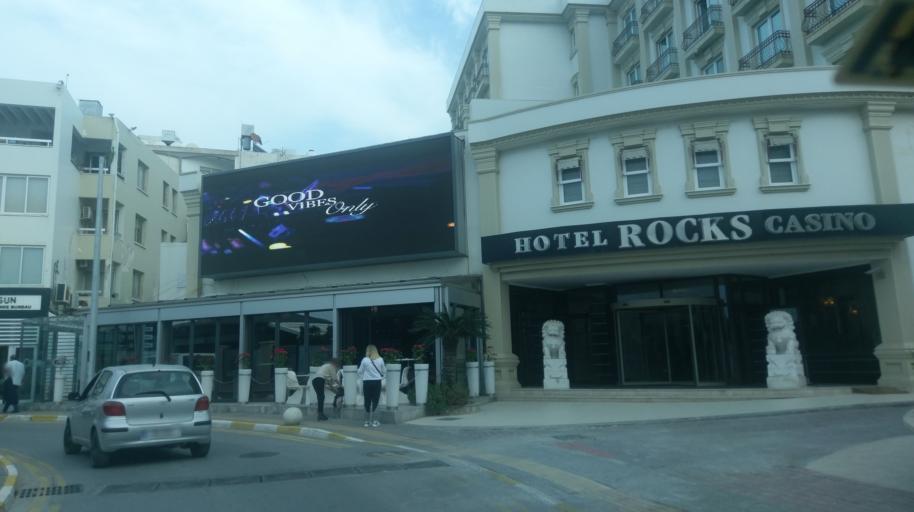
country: CY
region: Keryneia
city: Kyrenia
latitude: 35.3406
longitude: 33.3149
